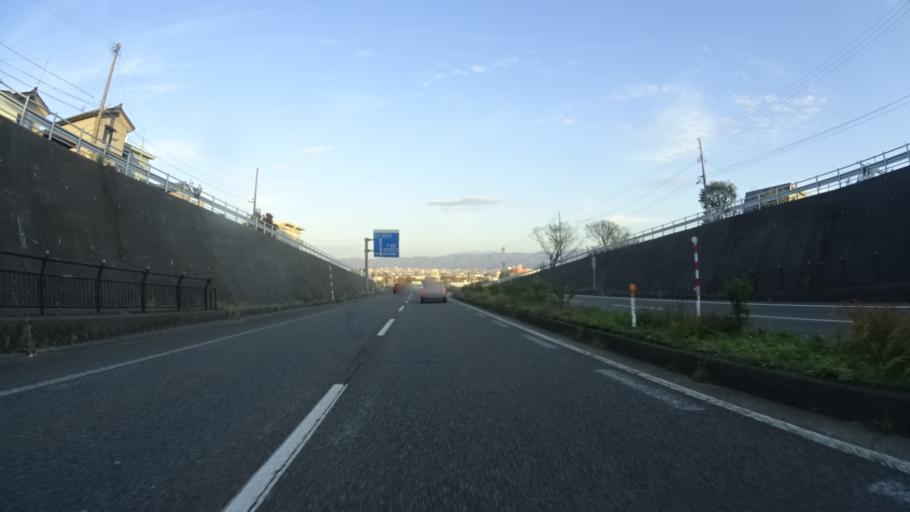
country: JP
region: Niigata
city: Nagaoka
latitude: 37.4445
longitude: 138.7829
